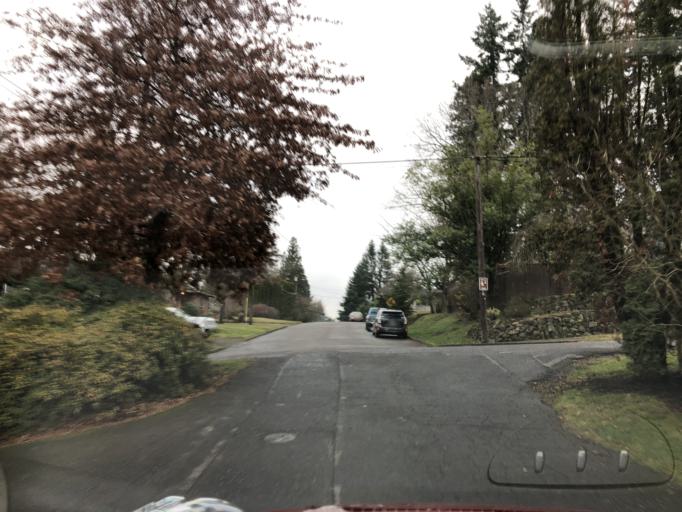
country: US
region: Oregon
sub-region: Washington County
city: Garden Home-Whitford
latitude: 45.4726
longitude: -122.7026
